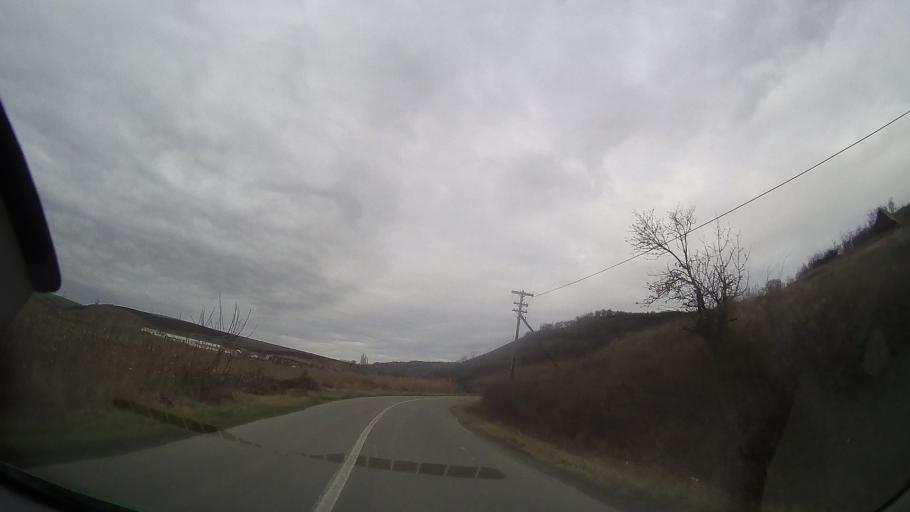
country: RO
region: Mures
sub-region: Comuna Faragau
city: Faragau
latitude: 46.7529
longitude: 24.5229
